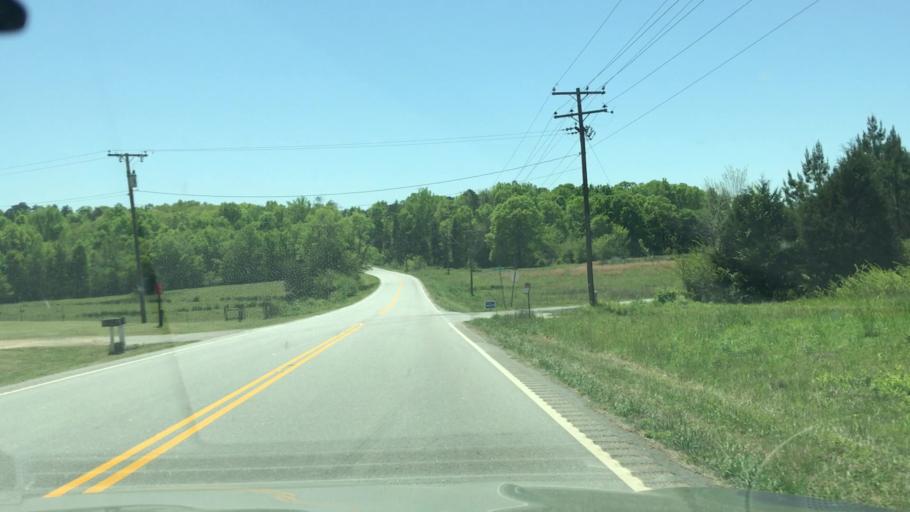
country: US
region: South Carolina
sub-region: Union County
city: Buffalo
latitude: 34.6811
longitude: -81.7281
